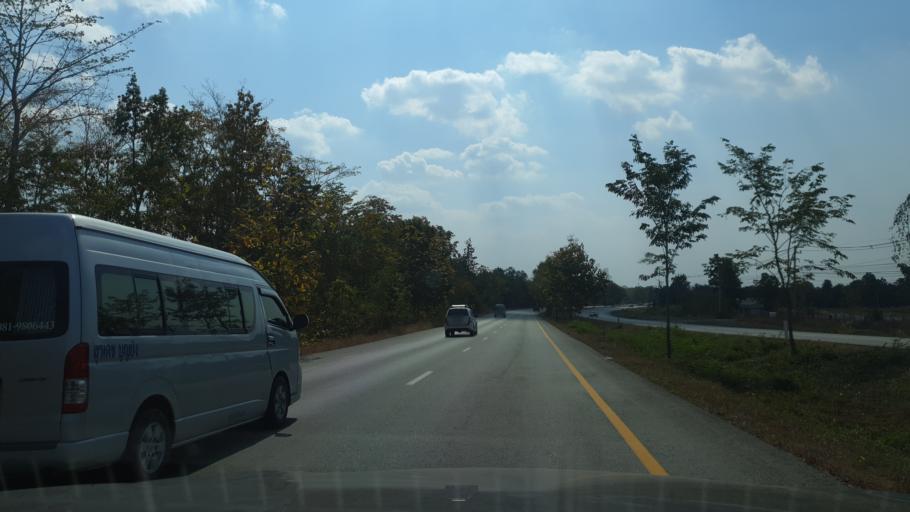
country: TH
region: Tak
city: Sam Ngao
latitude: 17.3055
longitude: 99.1479
